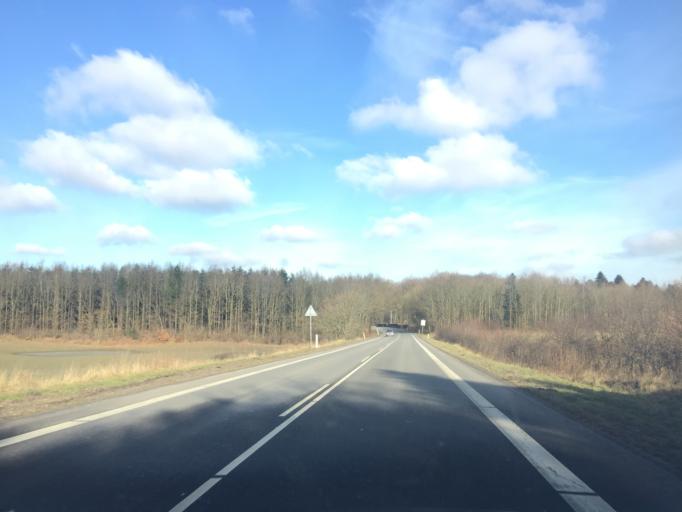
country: DK
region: South Denmark
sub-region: Assens Kommune
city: Vissenbjerg
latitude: 55.4292
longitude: 10.1828
